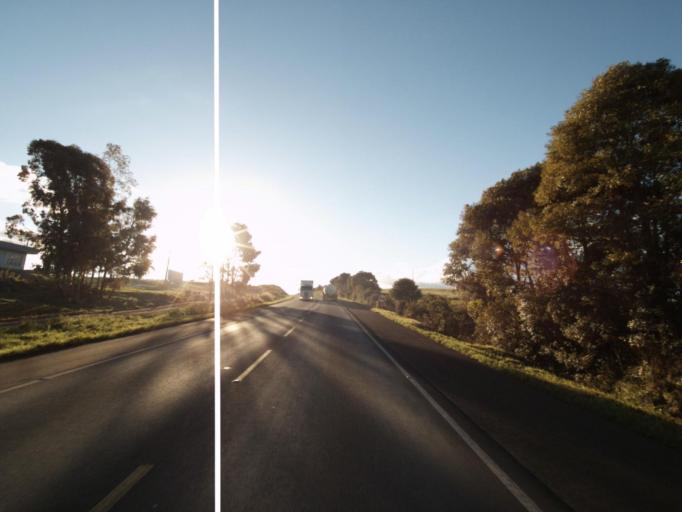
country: BR
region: Santa Catarina
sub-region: Campos Novos
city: Campos Novos
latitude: -27.3713
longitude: -51.2506
